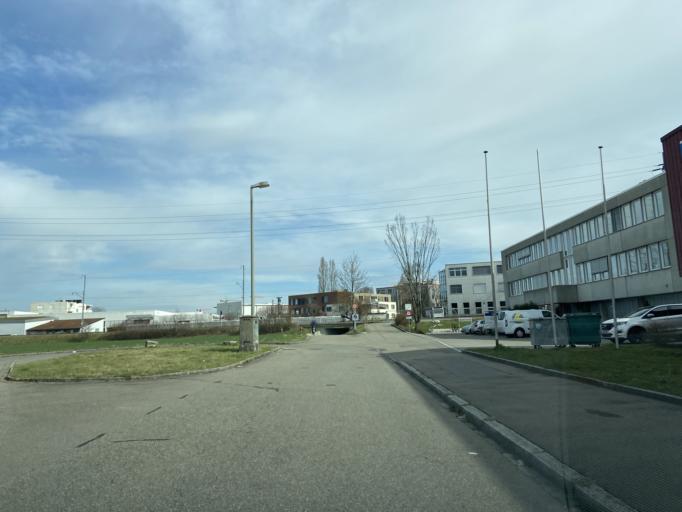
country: CH
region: Zurich
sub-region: Bezirk Winterthur
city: Seen (Kreis 3) / Waser
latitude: 47.4940
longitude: 8.7629
